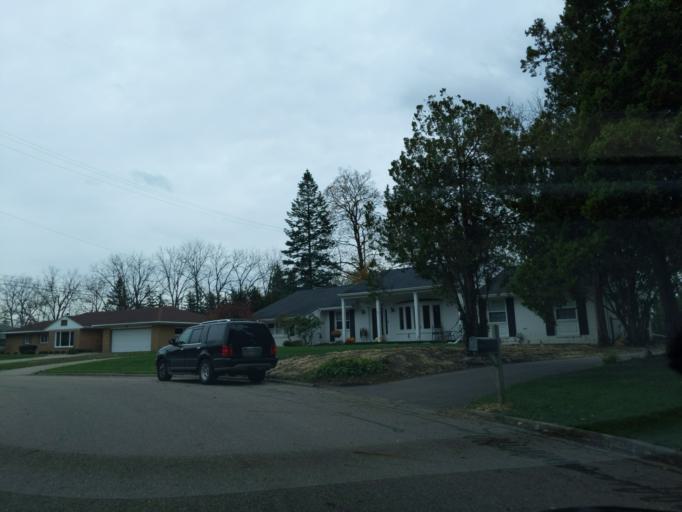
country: US
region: Michigan
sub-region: Ingham County
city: Edgemont Park
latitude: 42.7129
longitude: -84.5937
